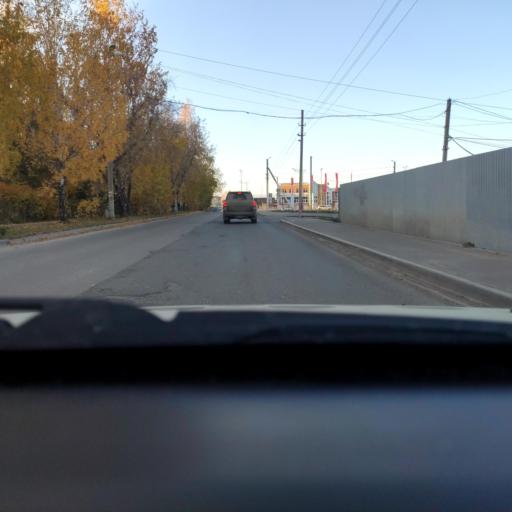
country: RU
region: Perm
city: Kondratovo
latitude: 57.9523
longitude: 56.1163
